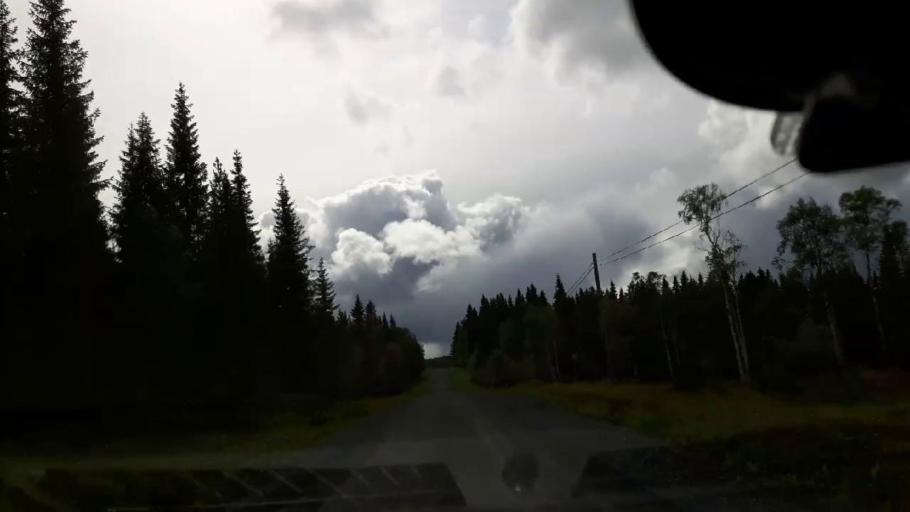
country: SE
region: Jaemtland
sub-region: Krokoms Kommun
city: Valla
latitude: 63.3618
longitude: 13.8623
